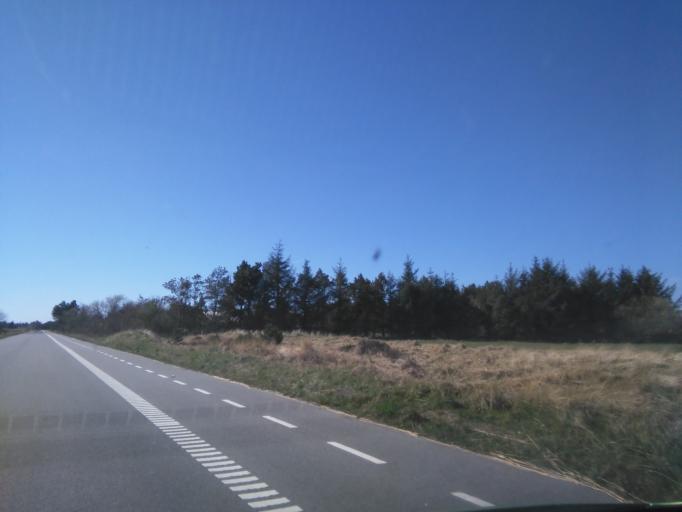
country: DK
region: South Denmark
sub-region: Varde Kommune
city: Oksbol
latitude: 55.5510
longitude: 8.1932
